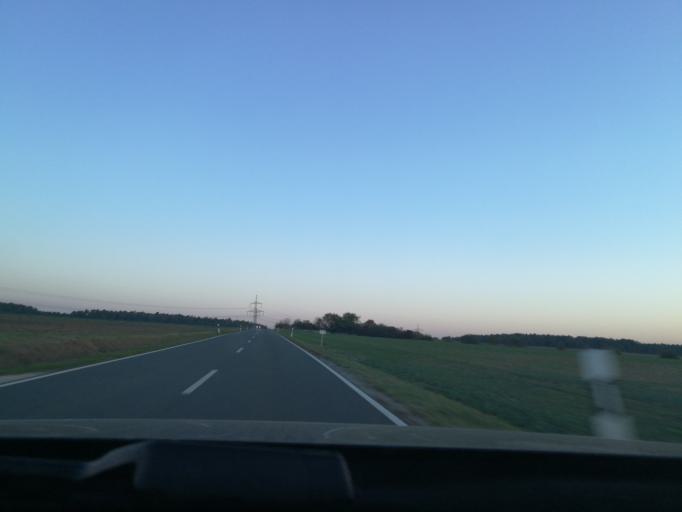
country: DE
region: Bavaria
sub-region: Regierungsbezirk Mittelfranken
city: Obermichelbach
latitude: 49.5374
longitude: 10.9110
